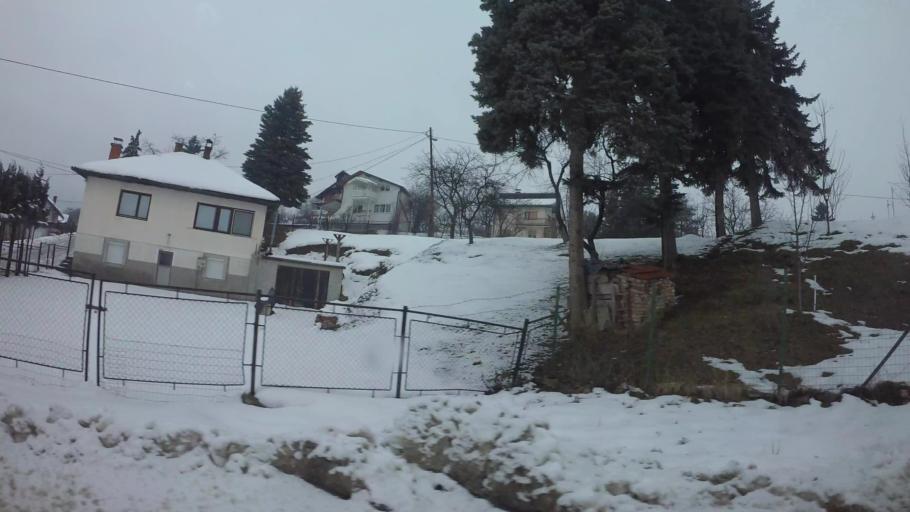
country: BA
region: Federation of Bosnia and Herzegovina
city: Hadzici
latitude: 43.8461
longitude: 18.2772
